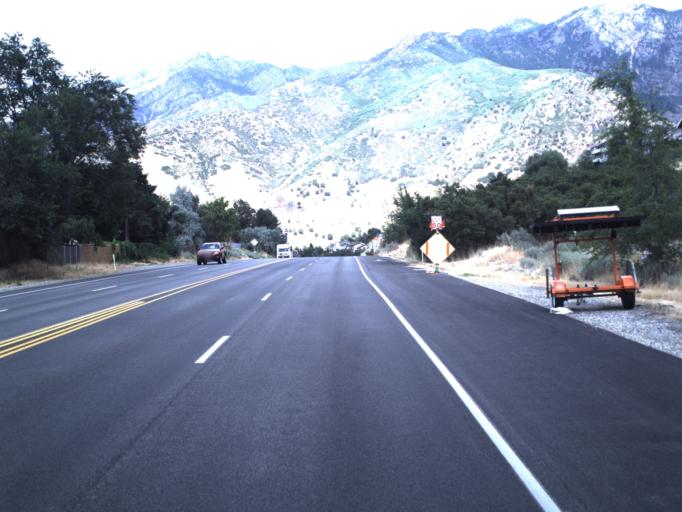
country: US
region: Utah
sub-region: Salt Lake County
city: Cottonwood Heights
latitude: 40.6109
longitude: -111.7910
